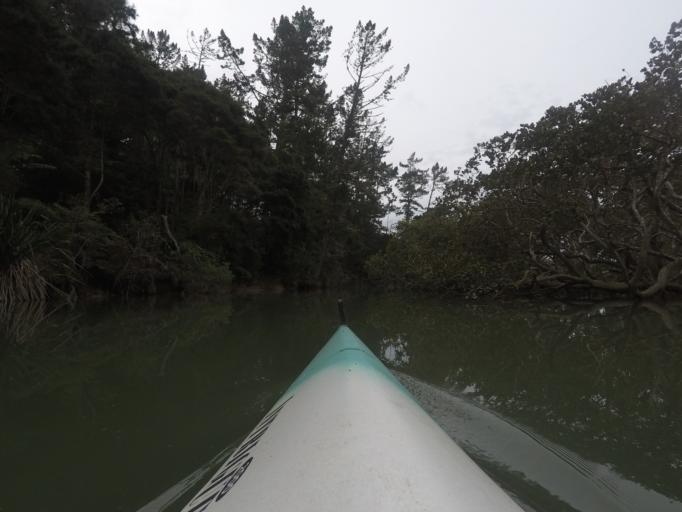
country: NZ
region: Auckland
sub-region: Auckland
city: Rothesay Bay
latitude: -36.6799
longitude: 174.7060
